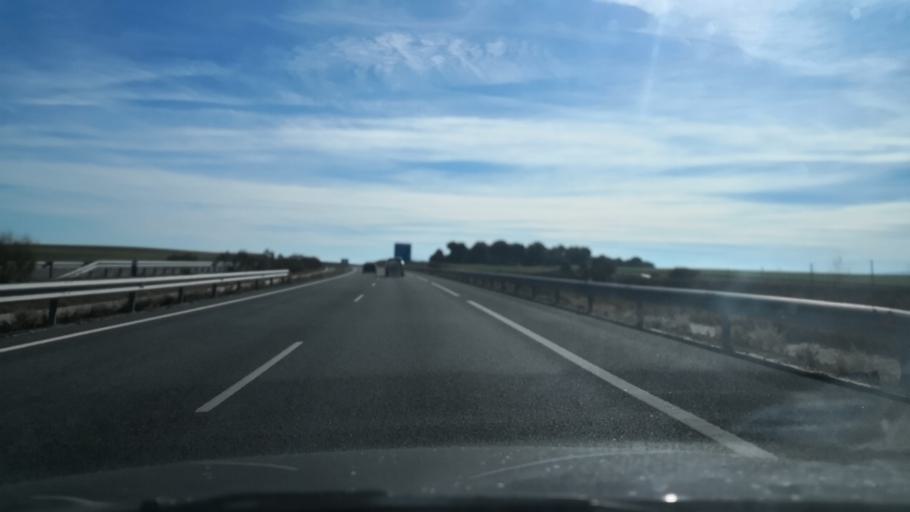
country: ES
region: Castille and Leon
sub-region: Provincia de Avila
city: Crespos
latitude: 40.8538
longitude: -4.9810
